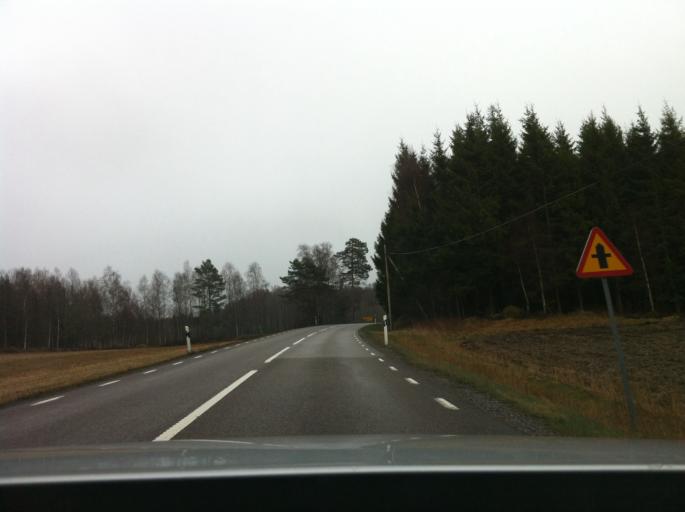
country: SE
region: Vaestra Goetaland
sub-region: Alingsas Kommun
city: Sollebrunn
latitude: 58.1337
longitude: 12.4799
